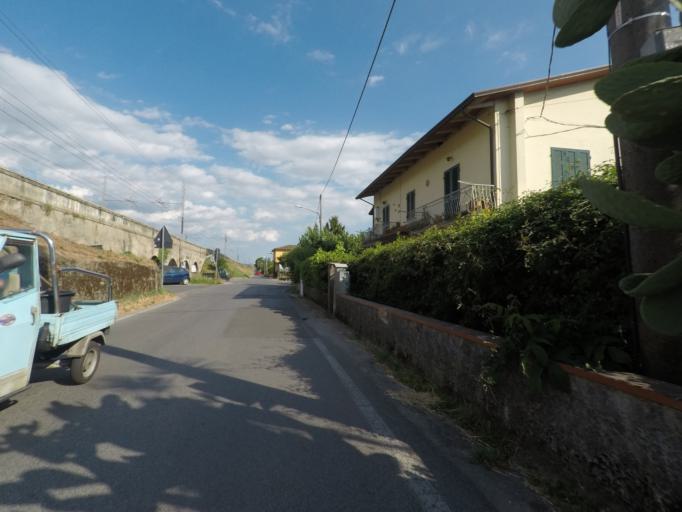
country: IT
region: Tuscany
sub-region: Provincia di Massa-Carrara
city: Capanne-Prato-Cinquale
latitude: 44.0138
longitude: 10.1494
